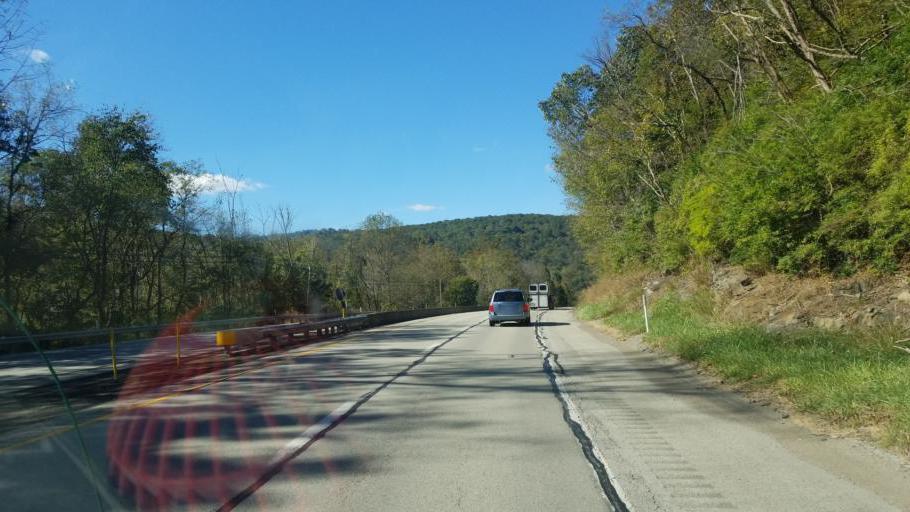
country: US
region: Pennsylvania
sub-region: Westmoreland County
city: Ligonier
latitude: 40.2649
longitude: -79.2859
